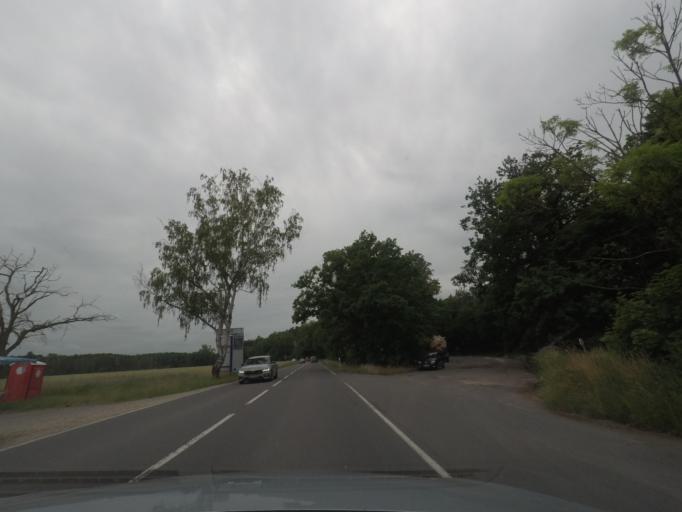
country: DE
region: Saxony-Anhalt
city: Haldensleben I
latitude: 52.2734
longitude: 11.3815
